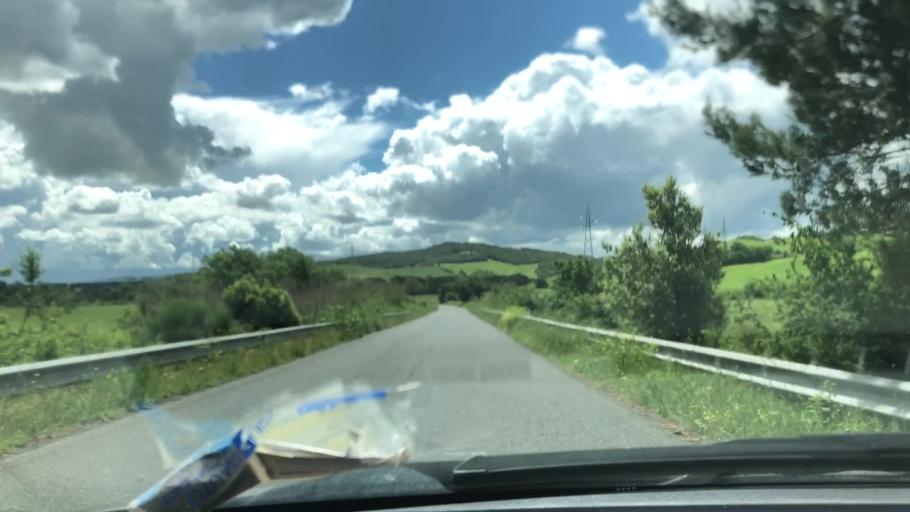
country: IT
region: Tuscany
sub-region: Province of Pisa
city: Saline
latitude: 43.3530
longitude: 10.7870
